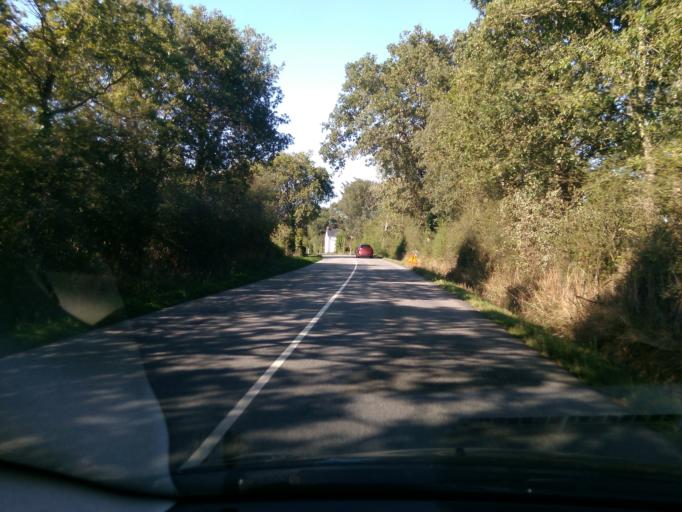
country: FR
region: Pays de la Loire
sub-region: Departement de la Loire-Atlantique
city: Quilly
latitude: 47.4341
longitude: -1.9258
